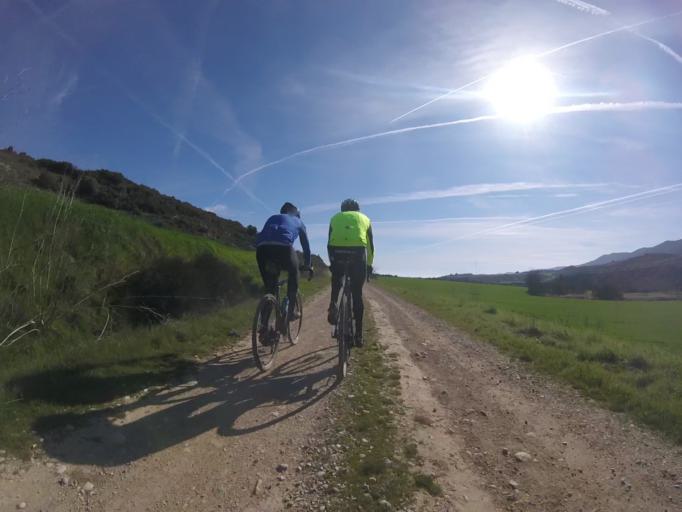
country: ES
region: Navarre
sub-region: Provincia de Navarra
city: Cirauqui
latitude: 42.6661
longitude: -1.9022
